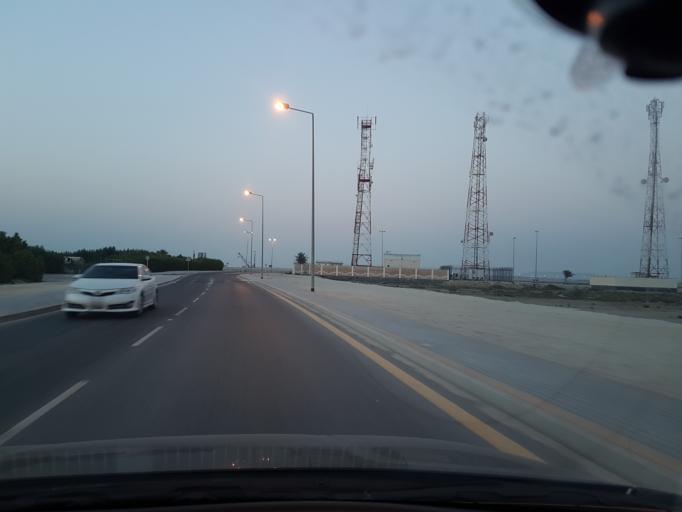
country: BH
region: Central Governorate
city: Dar Kulayb
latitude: 25.9943
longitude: 50.4677
